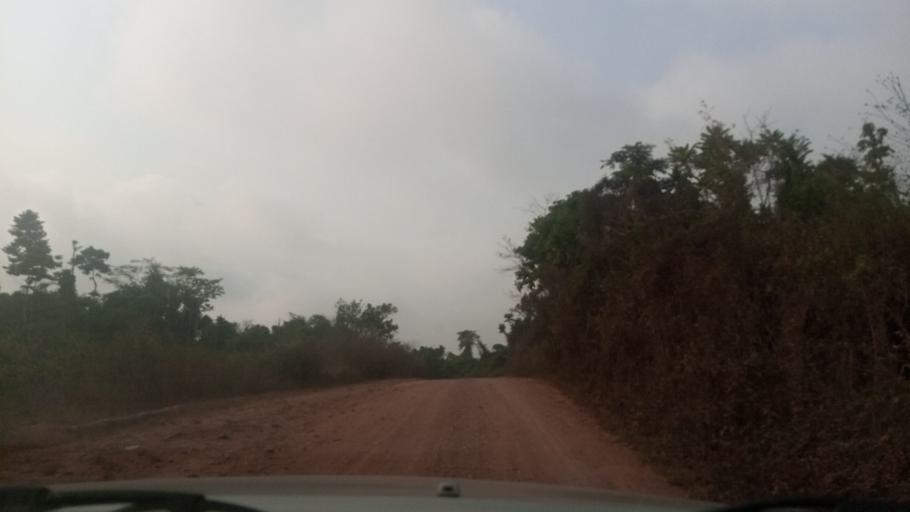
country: NG
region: Osun
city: Modakeke
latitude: 7.1270
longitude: 4.4086
